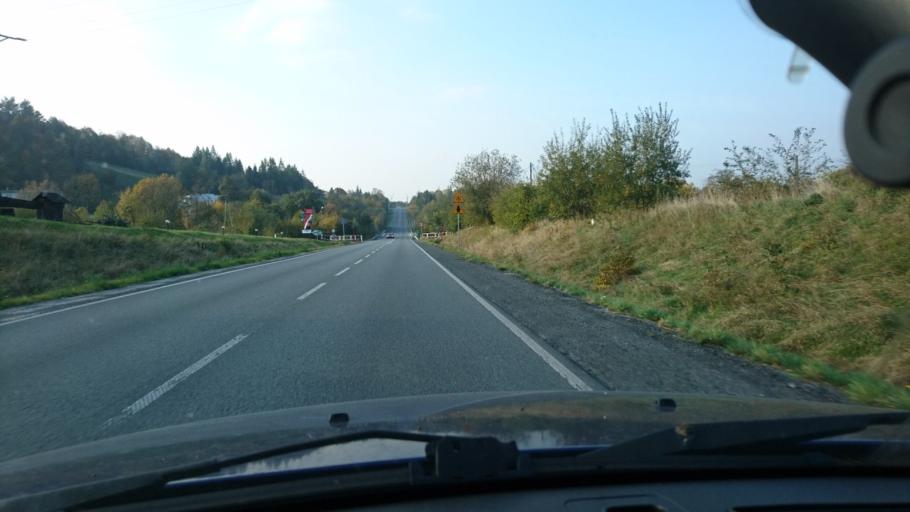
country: PL
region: Silesian Voivodeship
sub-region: Powiat cieszynski
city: Ustron
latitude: 49.7107
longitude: 18.8107
